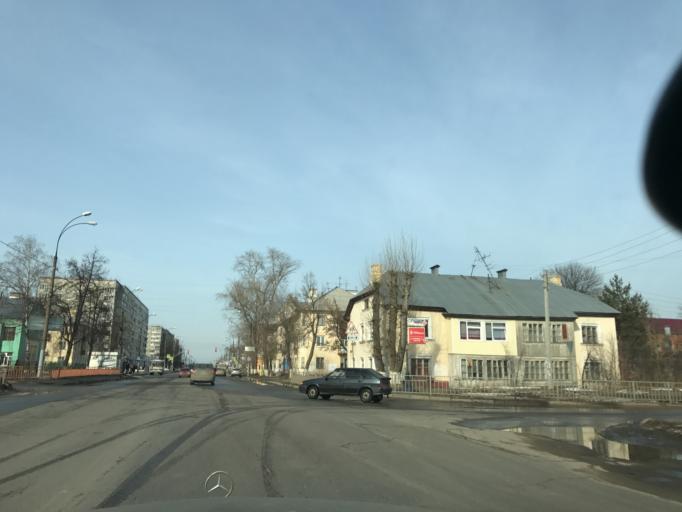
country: RU
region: Nizjnij Novgorod
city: Nizhniy Novgorod
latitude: 56.2680
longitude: 43.8902
